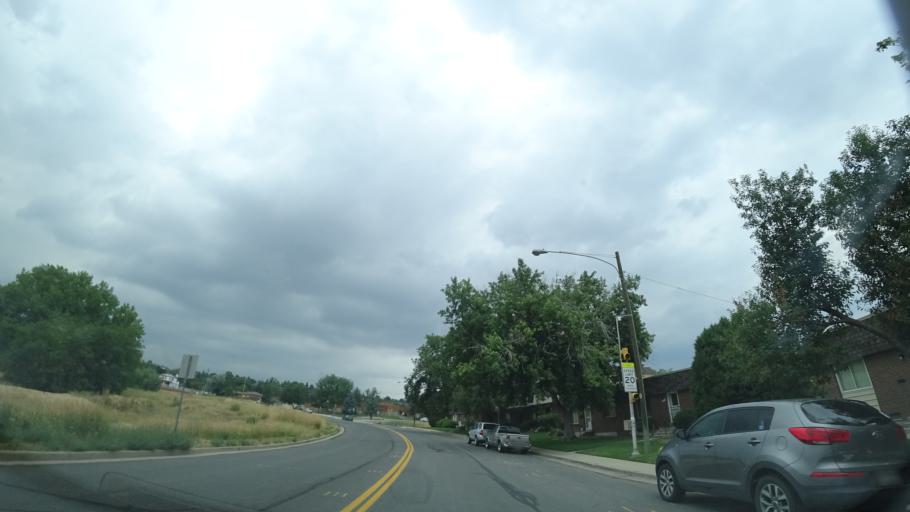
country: US
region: Colorado
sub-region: Jefferson County
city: West Pleasant View
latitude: 39.7016
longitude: -105.1450
